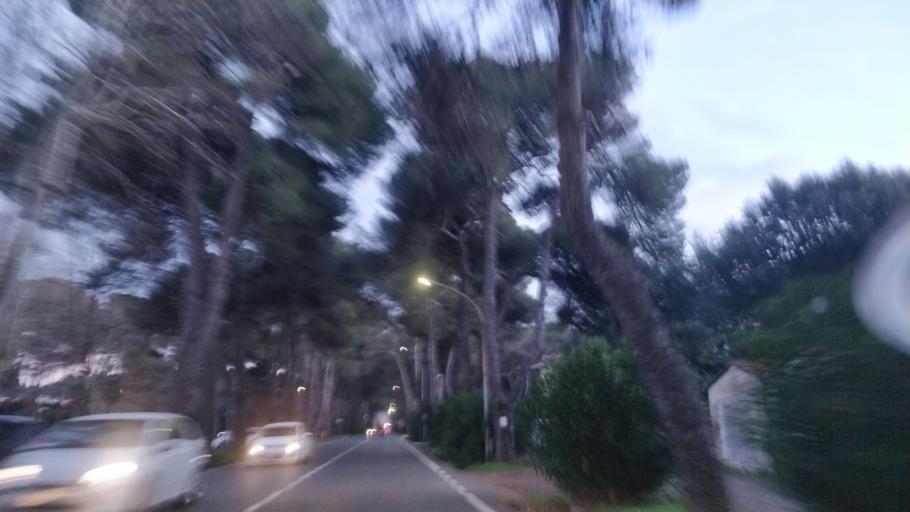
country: IT
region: Tuscany
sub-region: Provincia di Livorno
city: Rosignano Solvay-Castiglioncello
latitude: 43.3904
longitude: 10.4407
